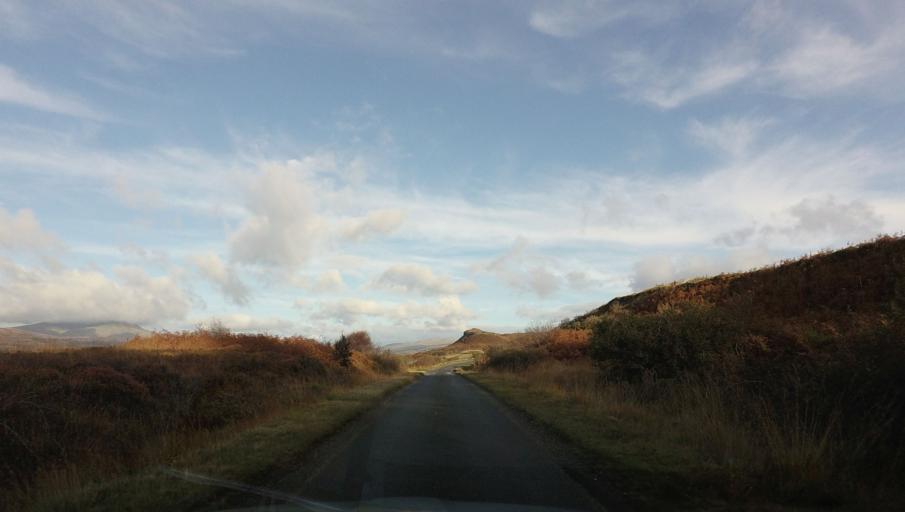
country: GB
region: Scotland
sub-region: Argyll and Bute
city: Isle Of Mull
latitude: 56.3364
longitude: -6.1490
